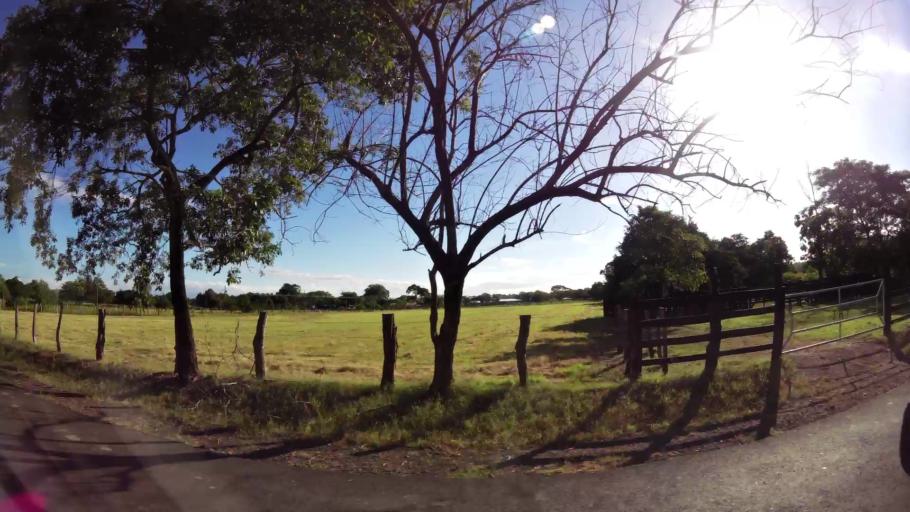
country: CR
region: Guanacaste
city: Sardinal
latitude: 10.5088
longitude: -85.6477
